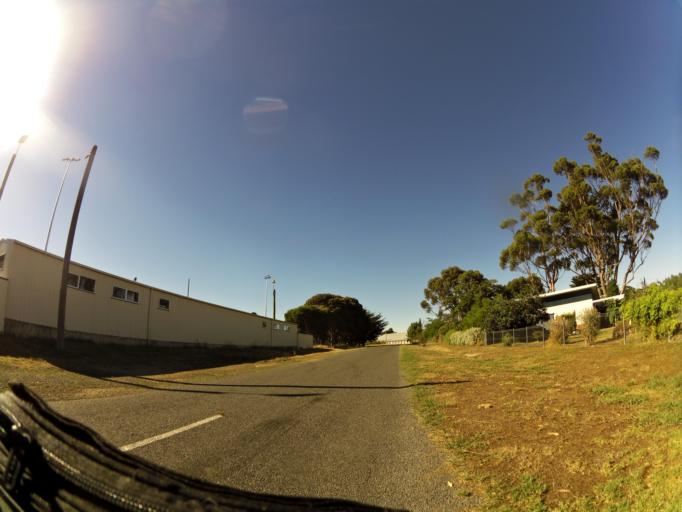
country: AU
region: Victoria
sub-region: Ballarat North
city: Delacombe
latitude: -37.6885
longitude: 143.3645
